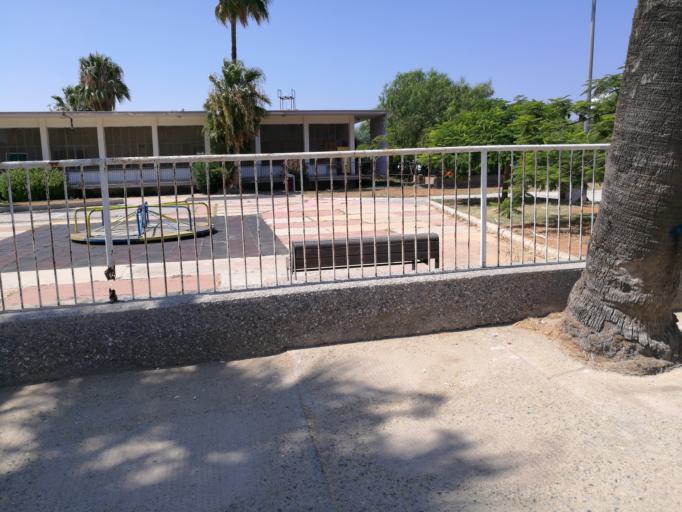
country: CY
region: Ammochostos
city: Famagusta
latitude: 35.1191
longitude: 33.9567
